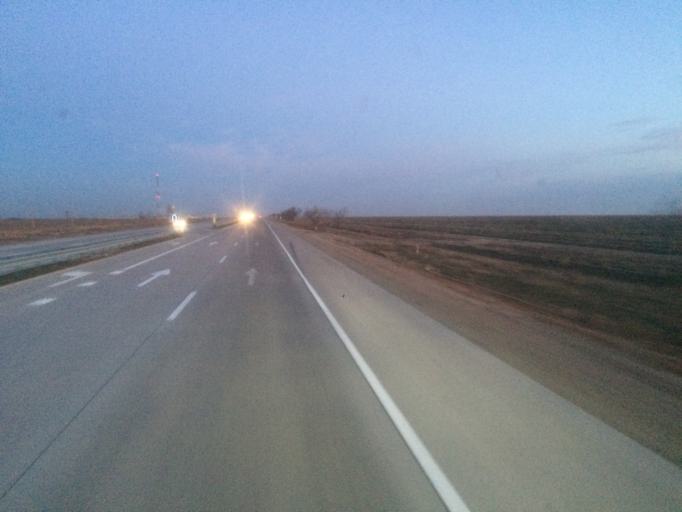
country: KZ
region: Ongtustik Qazaqstan
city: Temirlanovka
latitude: 42.8343
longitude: 69.1195
